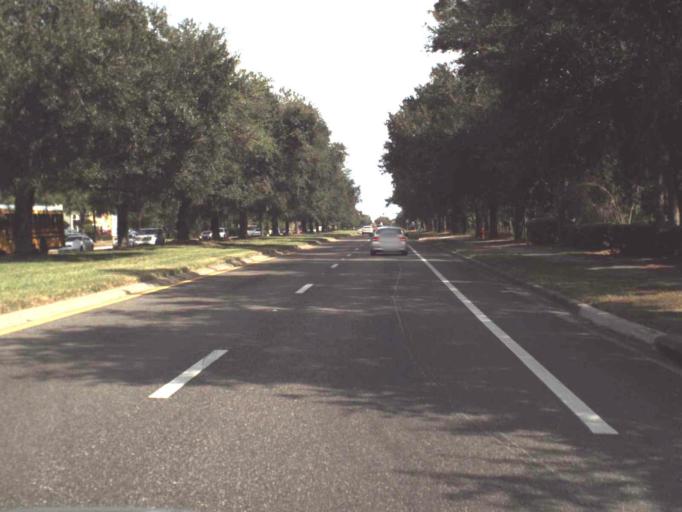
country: US
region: Florida
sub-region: Seminole County
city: Lake Mary
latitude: 28.7561
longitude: -81.3371
